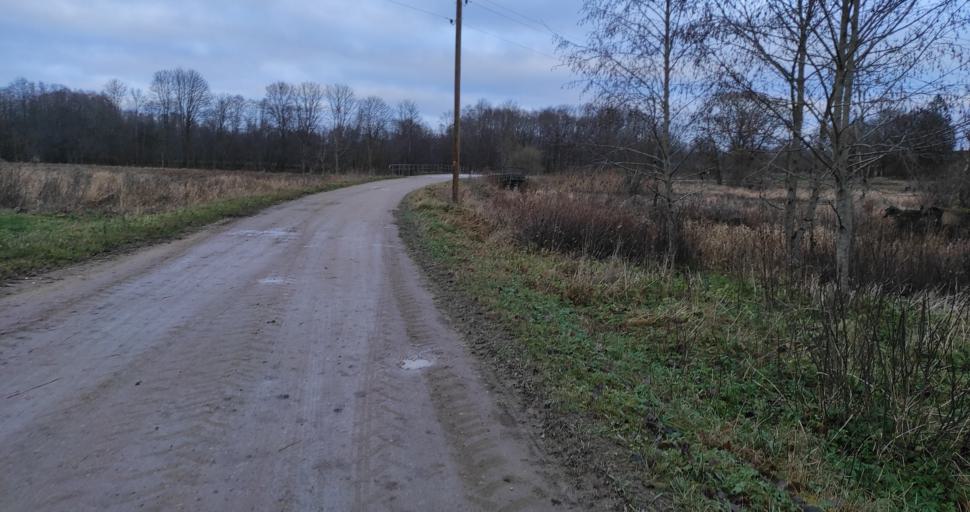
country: LV
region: Priekule
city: Priekule
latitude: 56.5065
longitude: 21.5050
